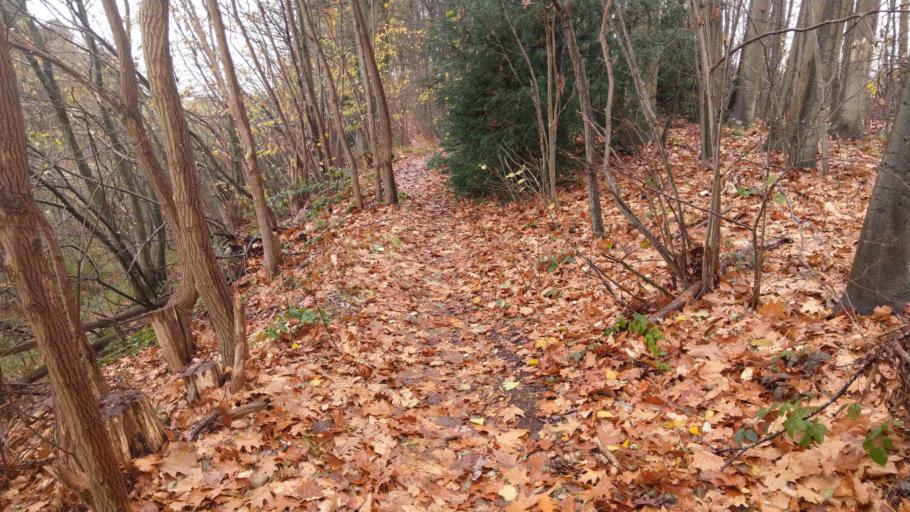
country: BE
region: Wallonia
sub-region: Province de Liege
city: La Calamine
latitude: 50.7384
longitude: 6.0496
